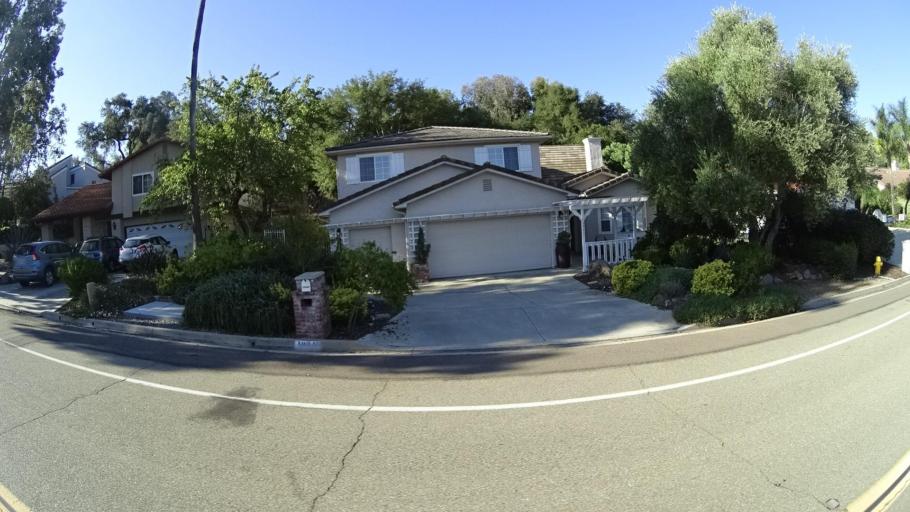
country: US
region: California
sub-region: San Diego County
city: Hidden Meadows
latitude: 33.2210
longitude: -117.0967
